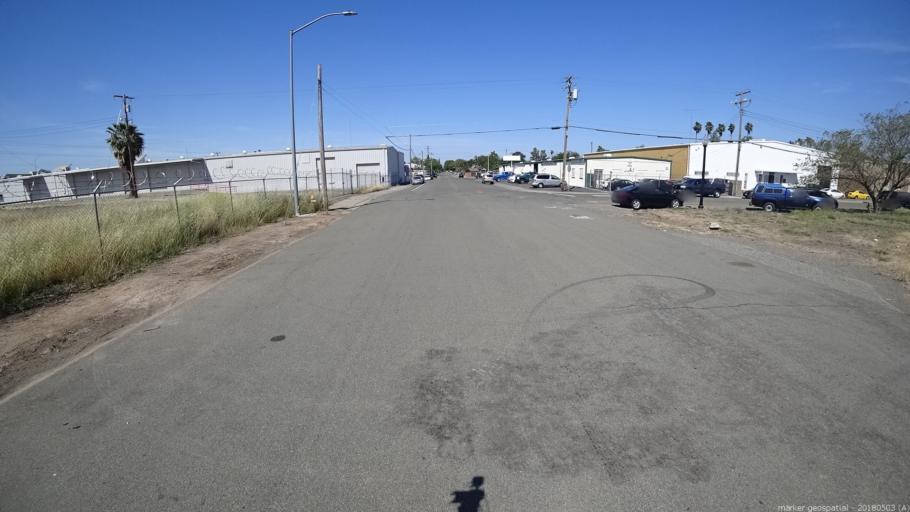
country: US
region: California
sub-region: Sacramento County
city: Sacramento
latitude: 38.6075
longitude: -121.4412
